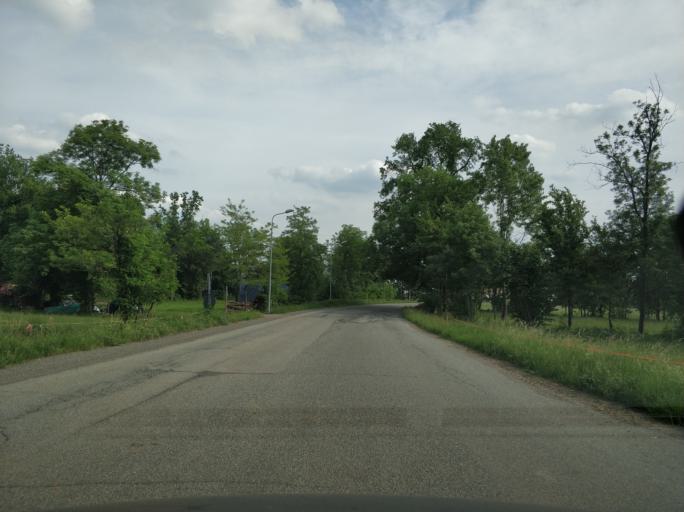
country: IT
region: Piedmont
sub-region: Provincia di Torino
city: Mathi
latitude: 45.2661
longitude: 7.5476
